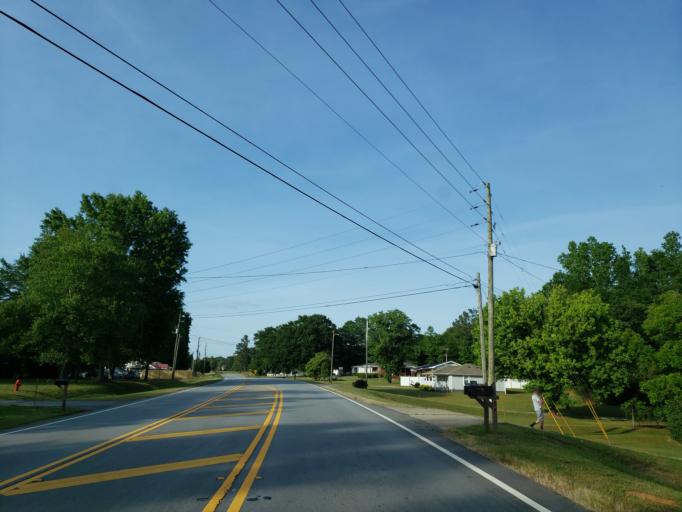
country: US
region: Georgia
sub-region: Carroll County
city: Bowdon
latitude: 33.4942
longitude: -85.2771
